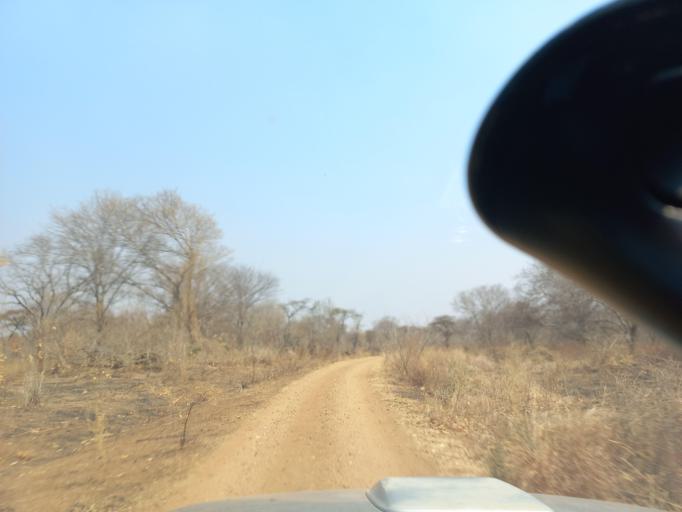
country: ZW
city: Chirundu
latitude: -15.8923
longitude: 28.7087
